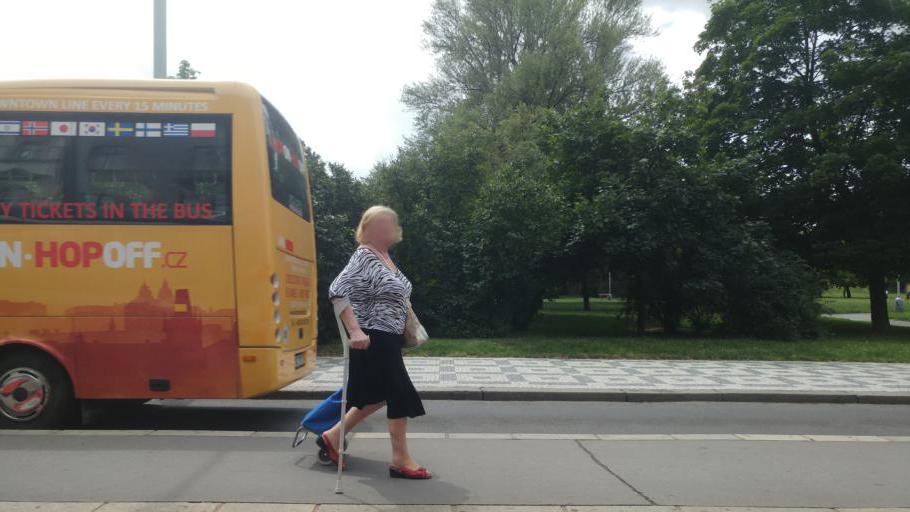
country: CZ
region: Praha
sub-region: Praha 8
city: Karlin
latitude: 50.0850
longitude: 14.4447
